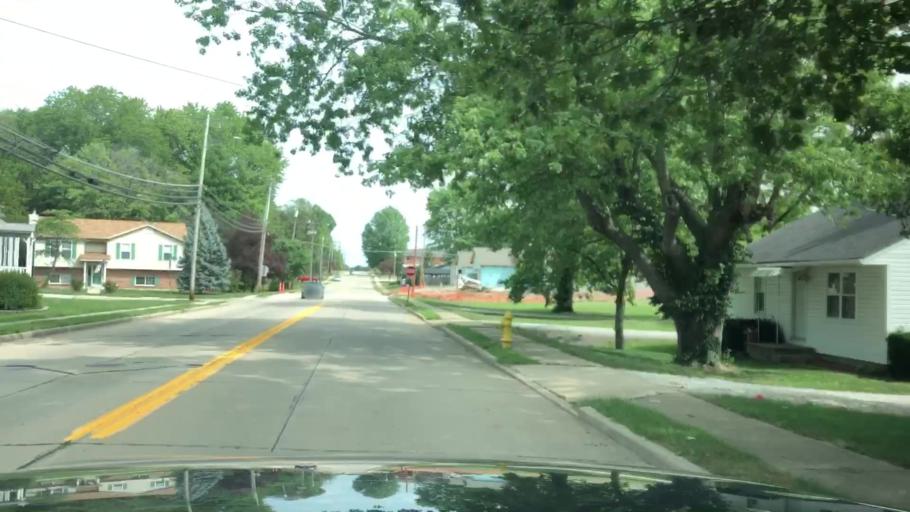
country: US
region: Missouri
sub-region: Saint Charles County
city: Wentzville
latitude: 38.8146
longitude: -90.8504
